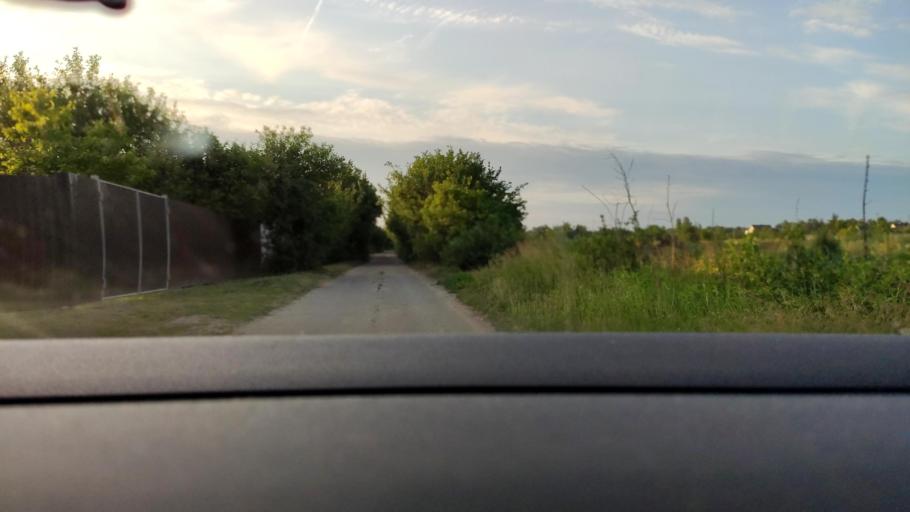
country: RU
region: Voronezj
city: Ramon'
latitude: 51.9082
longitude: 39.1771
